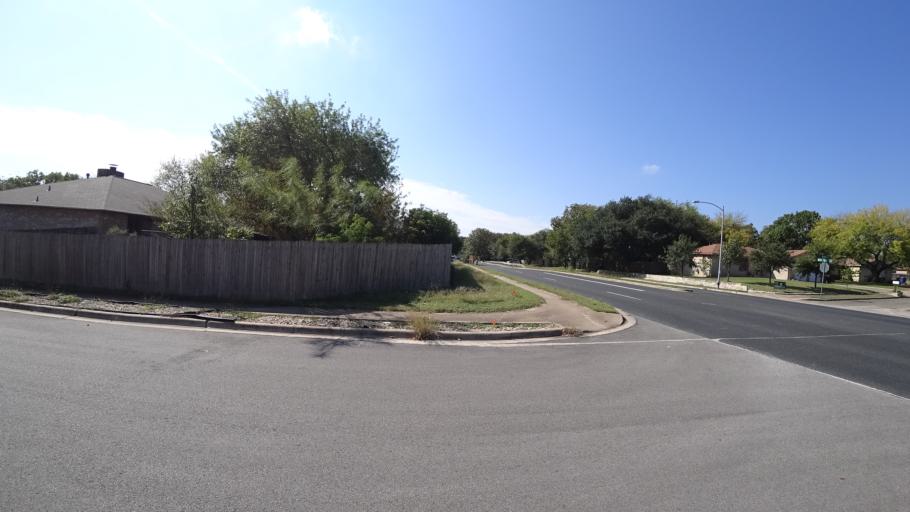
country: US
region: Texas
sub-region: Travis County
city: Rollingwood
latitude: 30.2151
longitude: -97.8139
